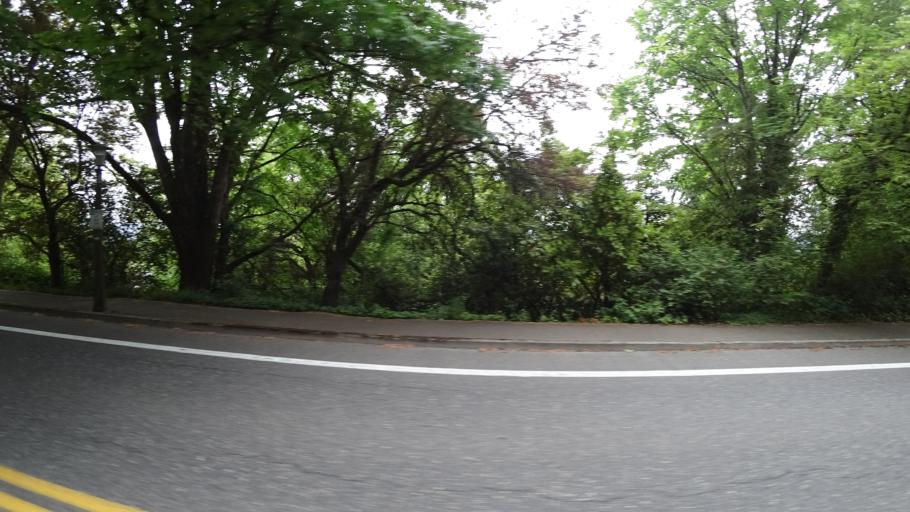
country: US
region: Oregon
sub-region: Multnomah County
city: Portland
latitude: 45.4923
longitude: -122.6815
